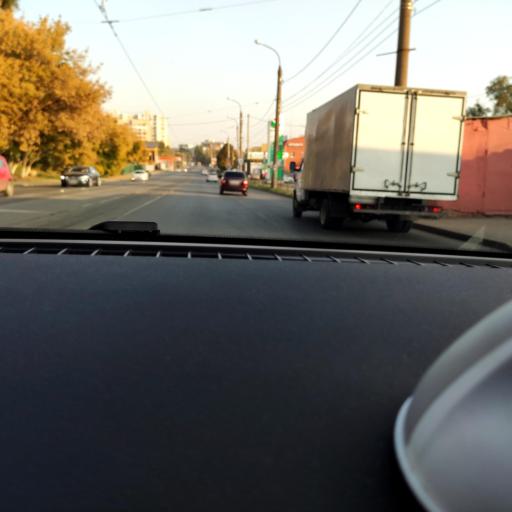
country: RU
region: Samara
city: Samara
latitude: 53.1942
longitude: 50.1627
